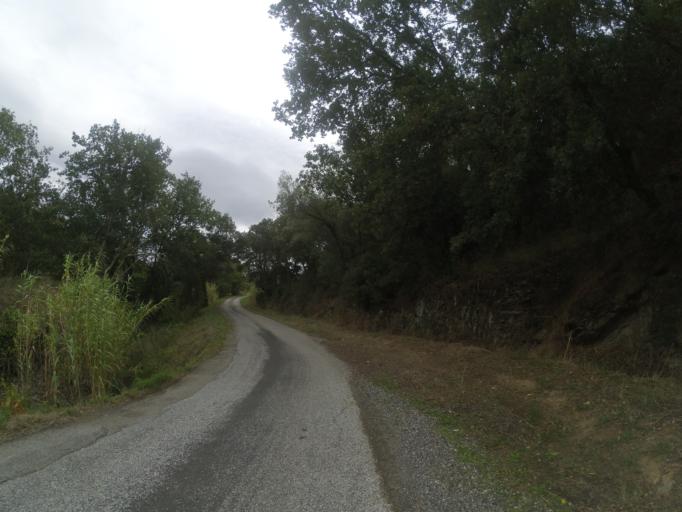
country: FR
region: Languedoc-Roussillon
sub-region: Departement des Pyrenees-Orientales
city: Estagel
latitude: 42.7432
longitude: 2.6782
